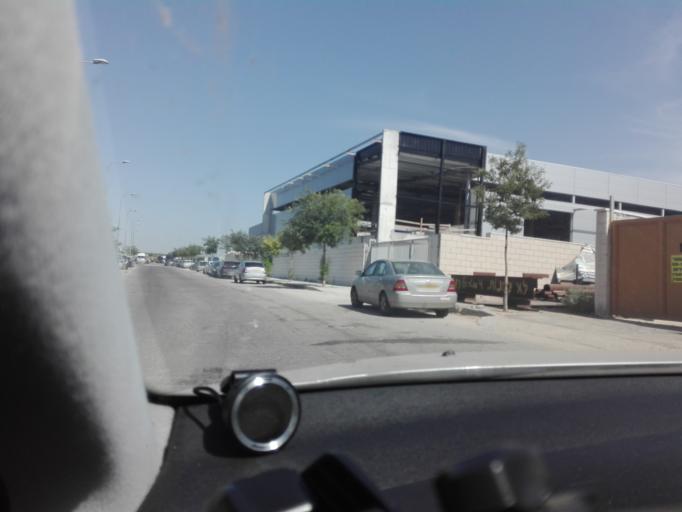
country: IL
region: Central District
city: Bene 'Ayish
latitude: 31.7214
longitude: 34.7593
